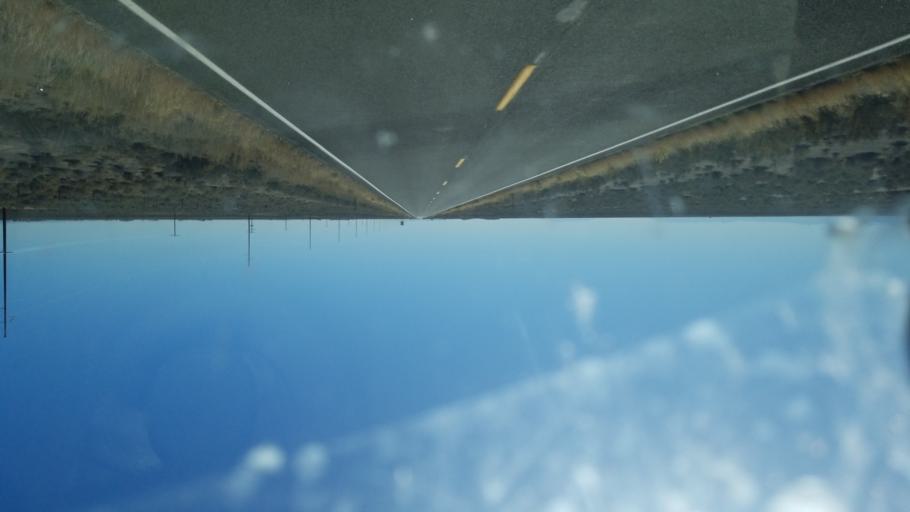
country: US
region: Colorado
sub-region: Saguache County
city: Center
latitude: 37.8944
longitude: -105.8968
